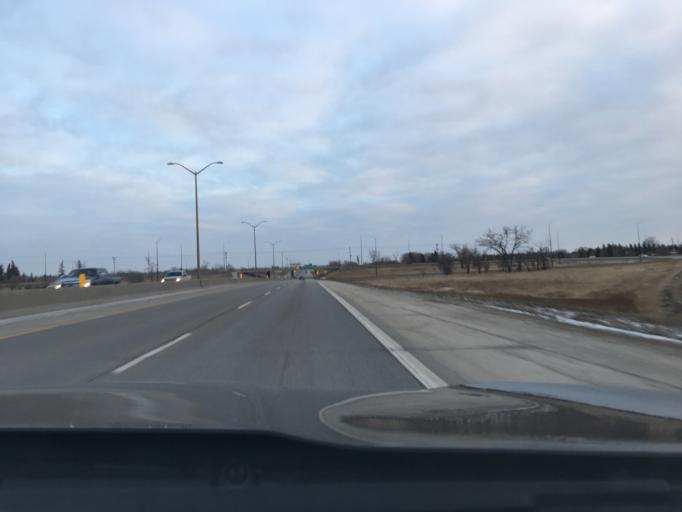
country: CA
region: Manitoba
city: Winnipeg
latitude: 49.9740
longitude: -97.0782
